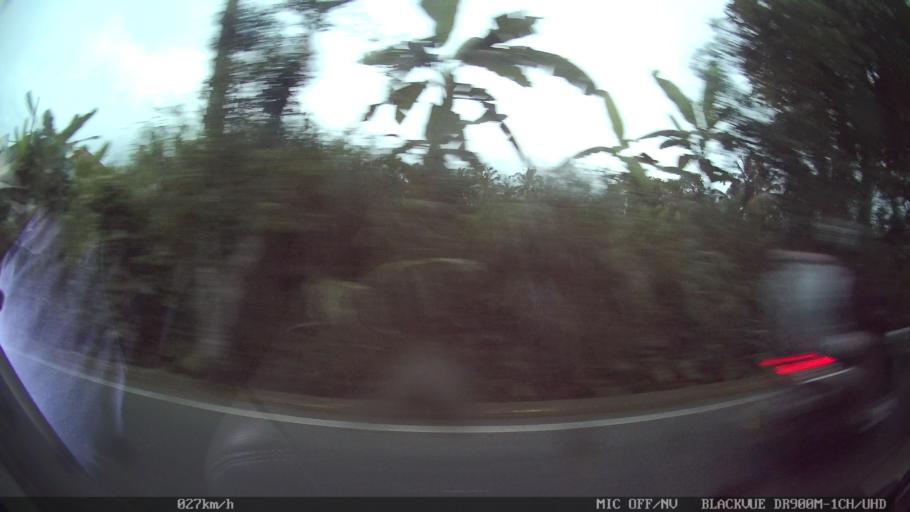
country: ID
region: Bali
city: Badung
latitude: -8.4202
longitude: 115.2452
